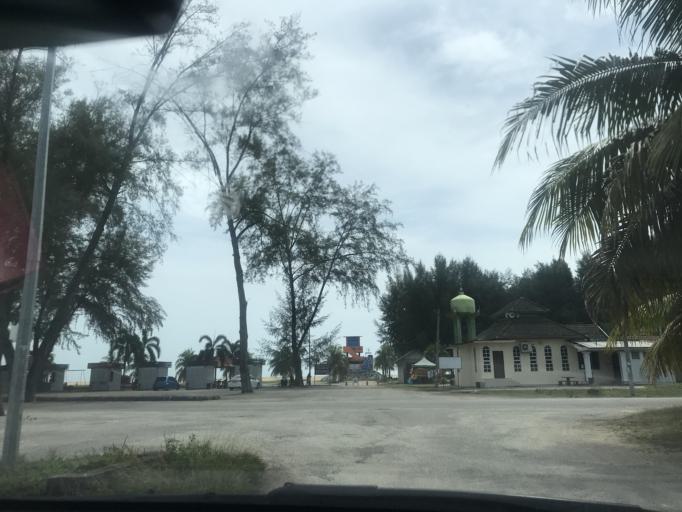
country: MY
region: Kelantan
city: Tumpat
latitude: 6.2236
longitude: 102.1176
